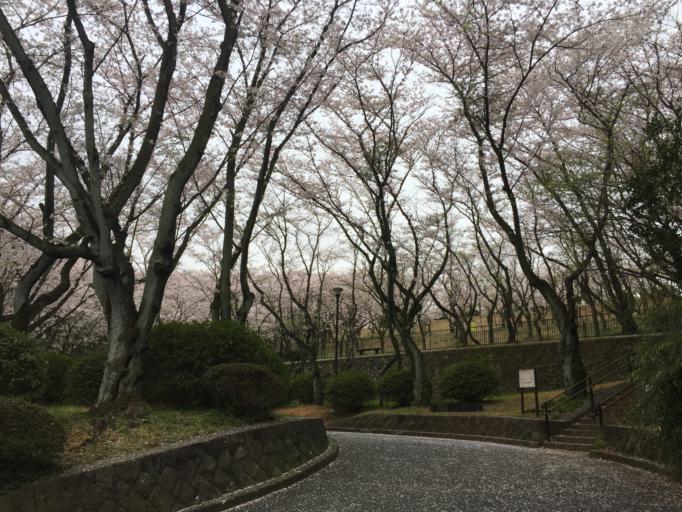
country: JP
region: Kanagawa
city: Yokohama
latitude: 35.4057
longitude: 139.6066
